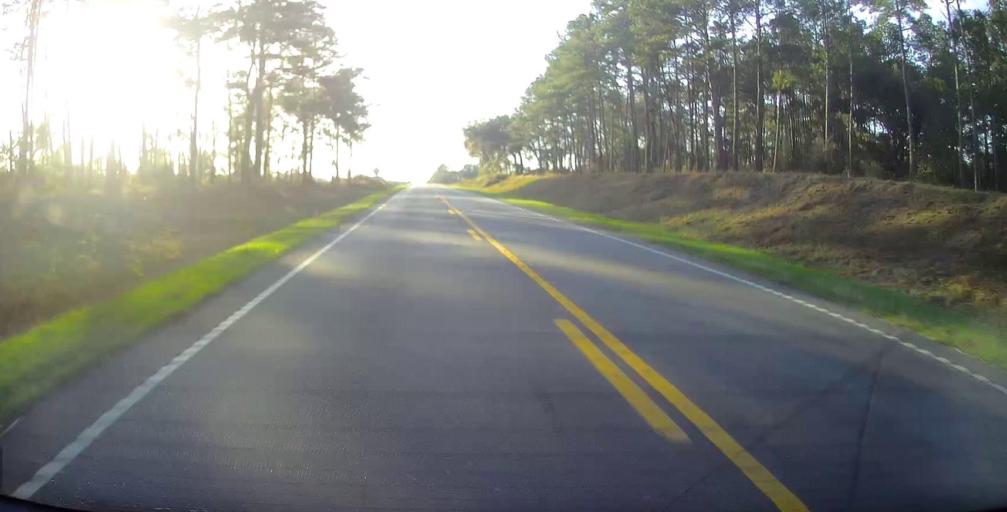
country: US
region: Georgia
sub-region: Evans County
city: Claxton
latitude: 32.1505
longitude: -81.7945
